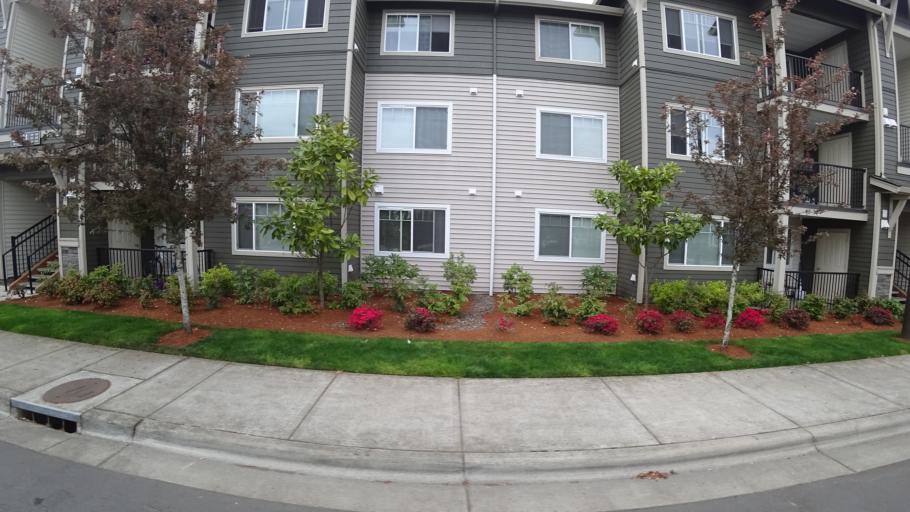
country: US
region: Oregon
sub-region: Washington County
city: Aloha
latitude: 45.5166
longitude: -122.8865
